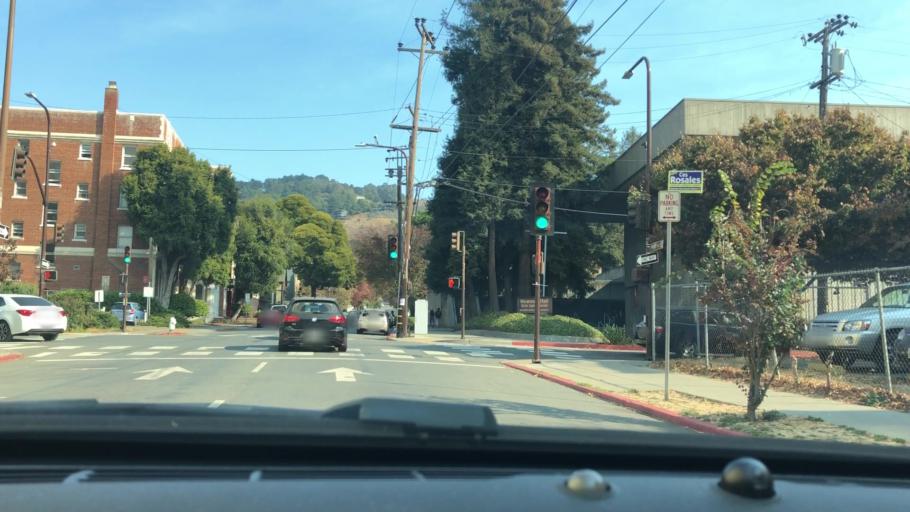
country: US
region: California
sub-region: Alameda County
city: Berkeley
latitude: 37.8657
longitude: -122.2542
